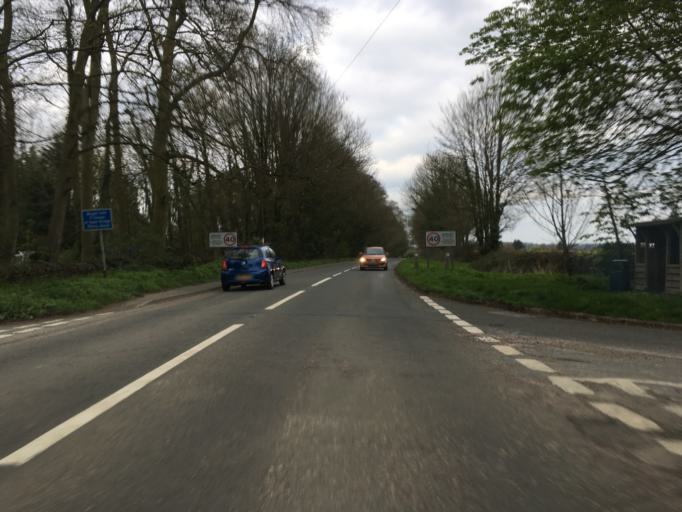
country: GB
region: England
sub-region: Gloucestershire
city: Northleach
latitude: 51.7570
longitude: -1.8498
